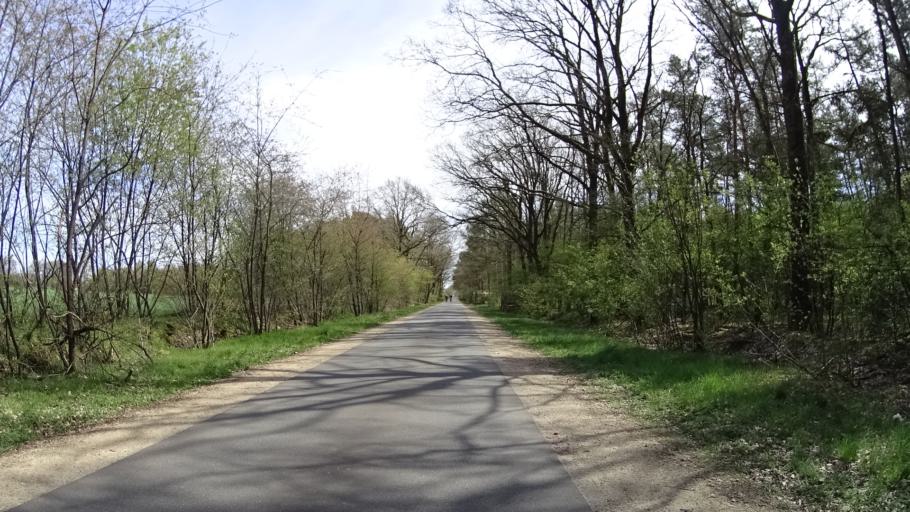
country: DE
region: Lower Saxony
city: Spelle
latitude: 52.3632
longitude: 7.4274
